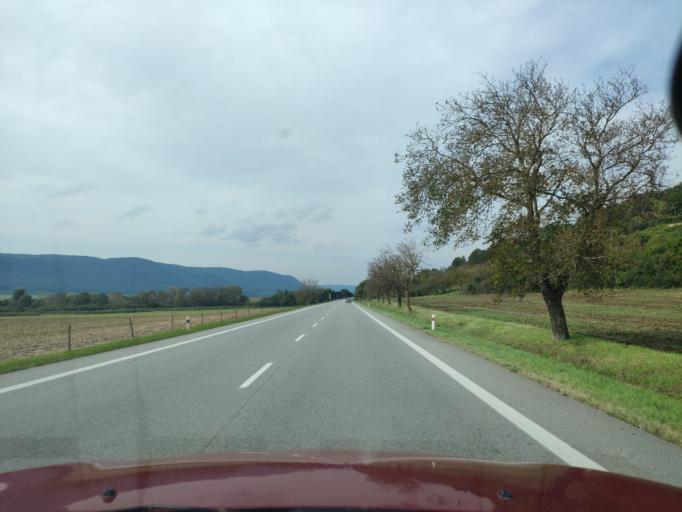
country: SK
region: Kosicky
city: Medzev
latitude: 48.6010
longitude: 20.8158
